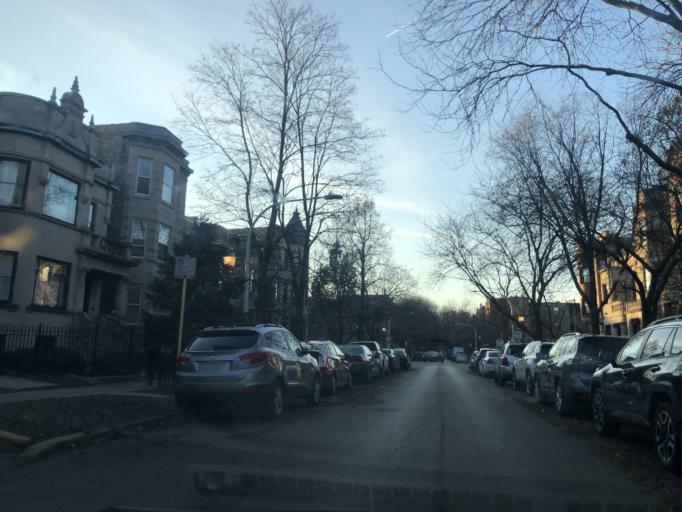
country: US
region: Illinois
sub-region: Cook County
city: Chicago
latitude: 41.9354
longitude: -87.6505
